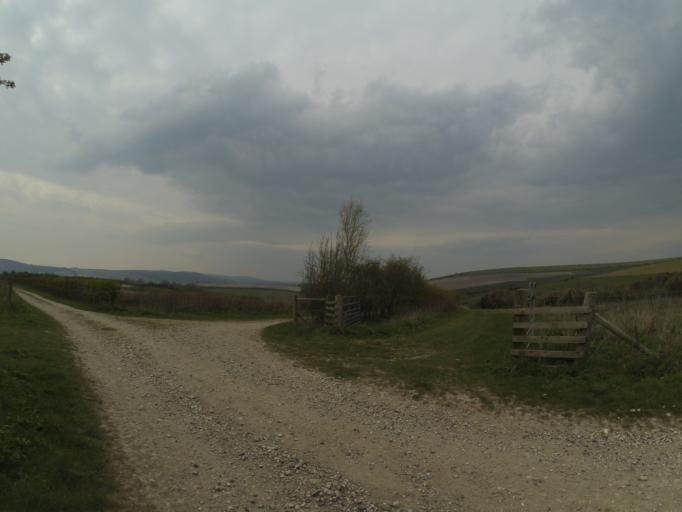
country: GB
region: England
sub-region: West Sussex
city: Arundel
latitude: 50.8924
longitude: -0.5162
